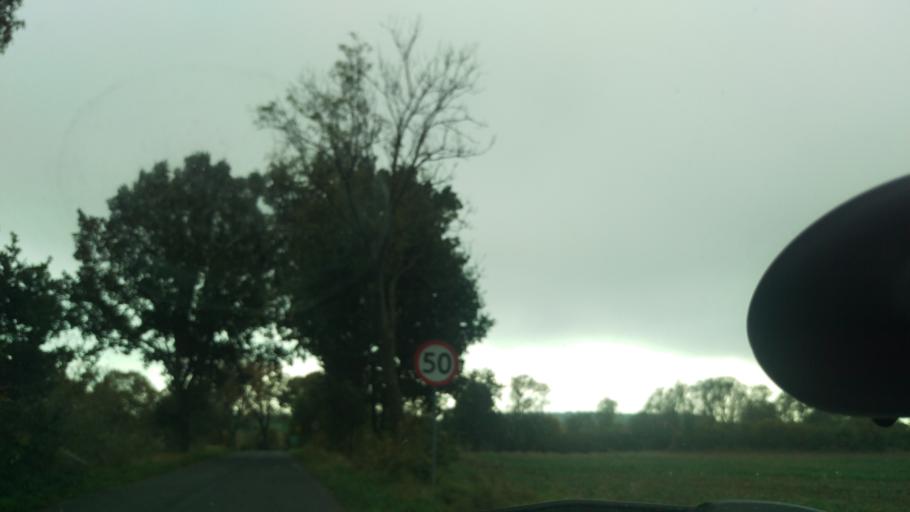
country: PL
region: West Pomeranian Voivodeship
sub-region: Powiat mysliborski
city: Barlinek
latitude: 53.0425
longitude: 15.1574
